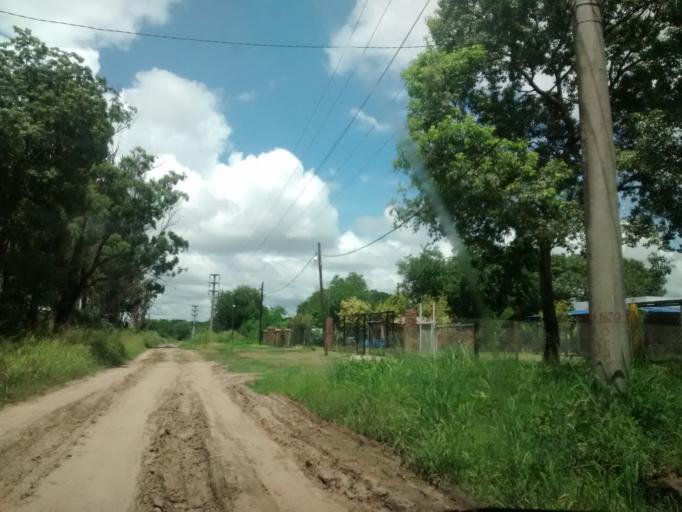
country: AR
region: Chaco
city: Fontana
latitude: -27.4111
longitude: -58.9852
